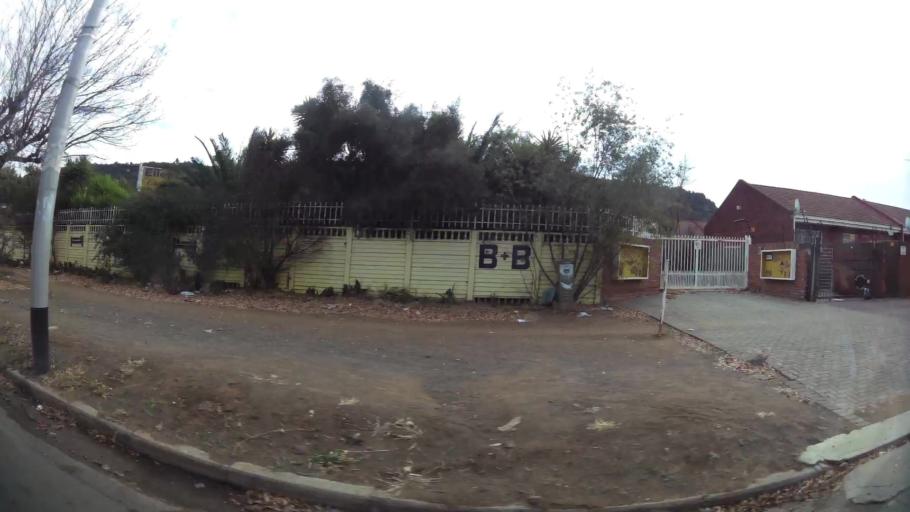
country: ZA
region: Orange Free State
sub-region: Mangaung Metropolitan Municipality
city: Bloemfontein
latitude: -29.0986
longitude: 26.2439
